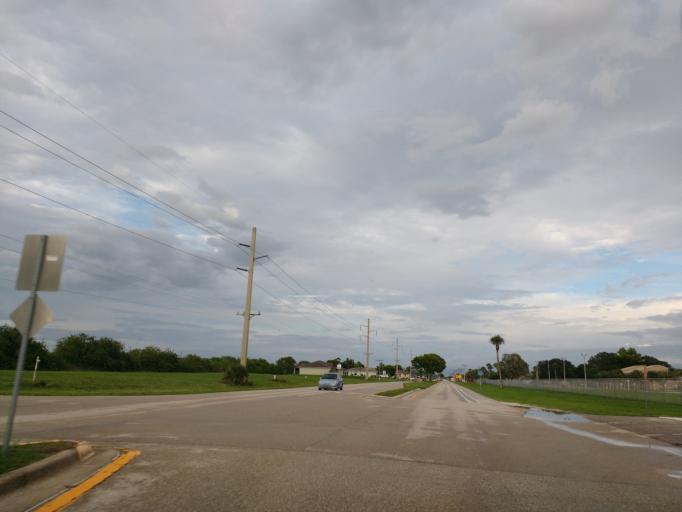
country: US
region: Florida
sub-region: Lee County
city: Cape Coral
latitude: 26.6227
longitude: -82.0190
